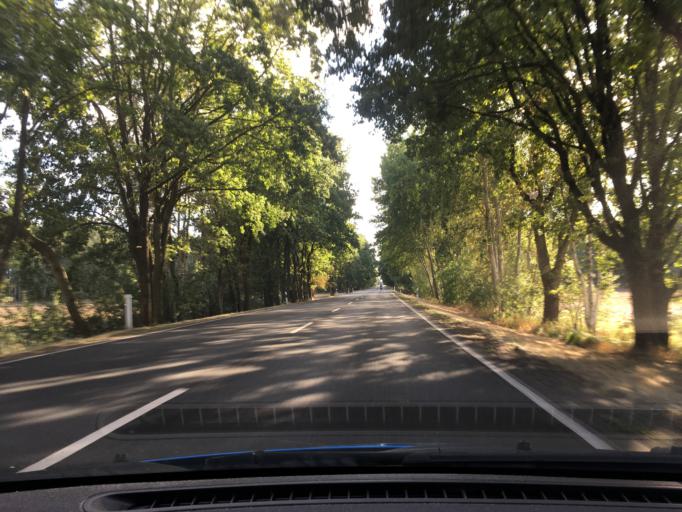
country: DE
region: Mecklenburg-Vorpommern
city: Gross Laasch
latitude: 53.3517
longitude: 11.5349
